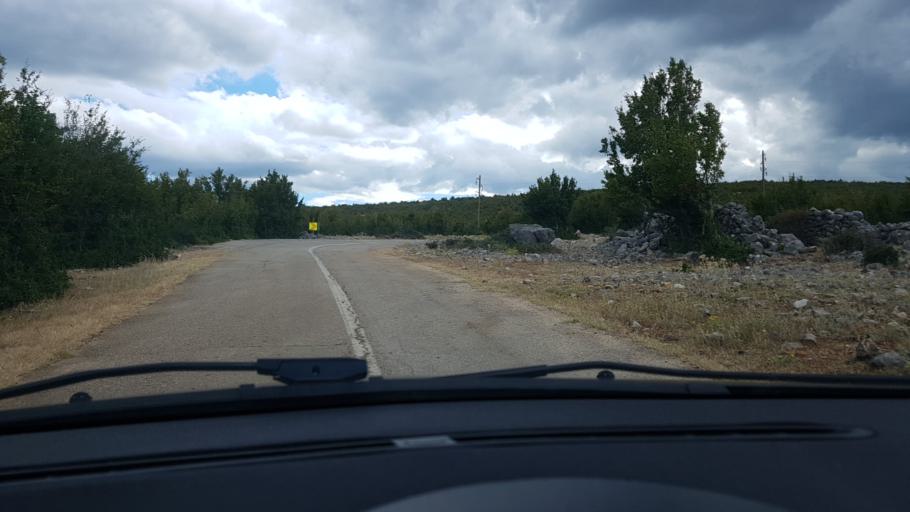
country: HR
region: Zadarska
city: Gracac
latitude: 44.1845
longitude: 15.8981
